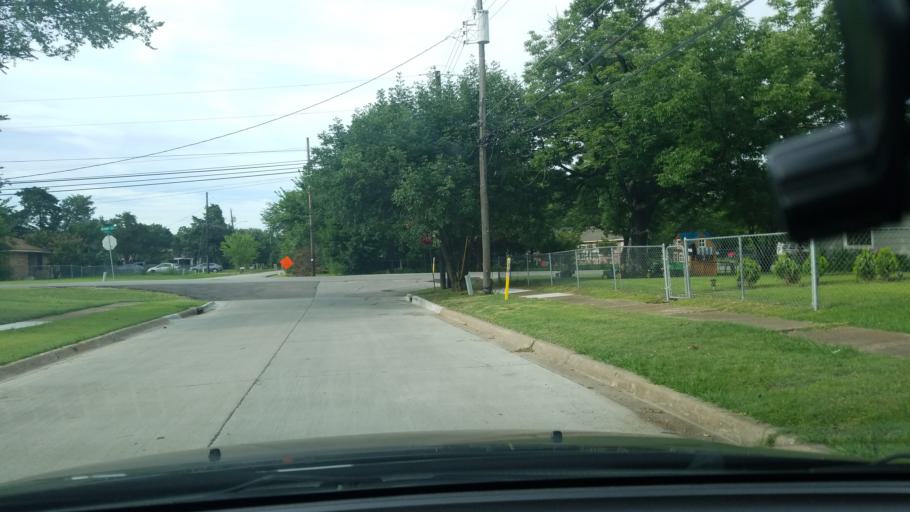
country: US
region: Texas
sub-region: Dallas County
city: Balch Springs
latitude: 32.7597
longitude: -96.6619
